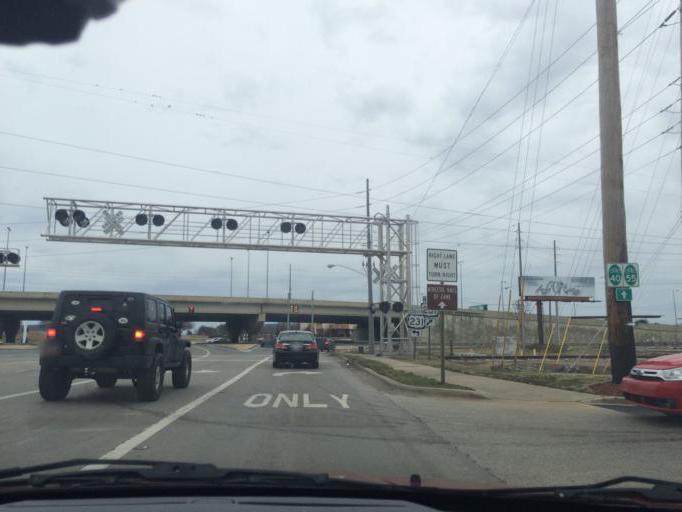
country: US
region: Alabama
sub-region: Madison County
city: Huntsville
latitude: 34.6908
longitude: -86.5793
